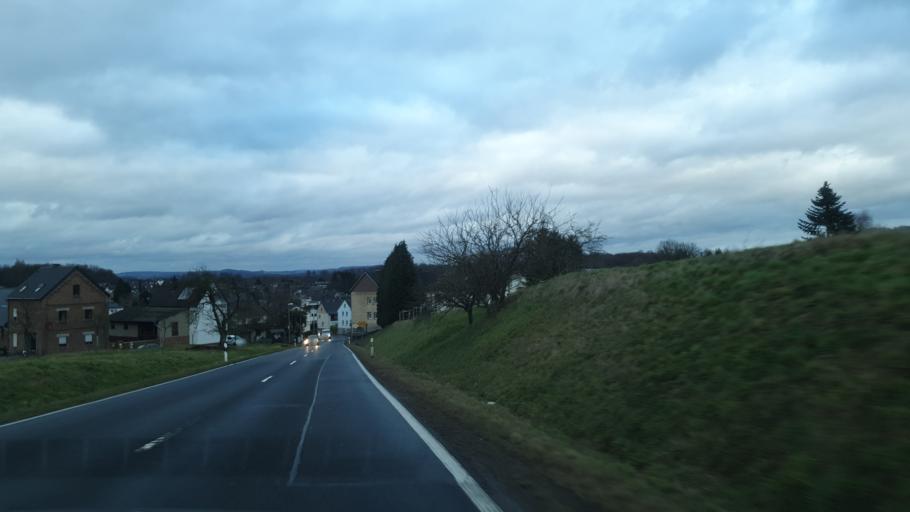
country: DE
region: Rheinland-Pfalz
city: Eppenrod
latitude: 50.4010
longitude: 7.9290
